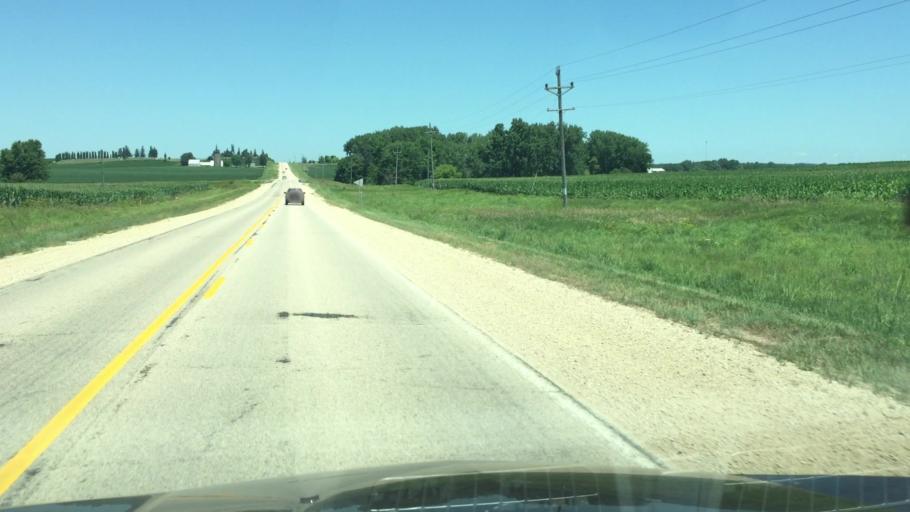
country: US
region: Iowa
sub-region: Cedar County
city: Mechanicsville
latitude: 41.9699
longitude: -91.1419
